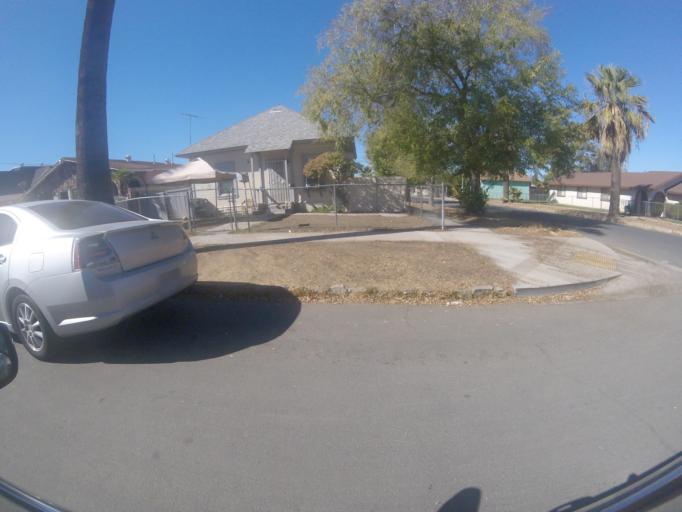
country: US
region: California
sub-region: San Bernardino County
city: Redlands
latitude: 34.0651
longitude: -117.1836
